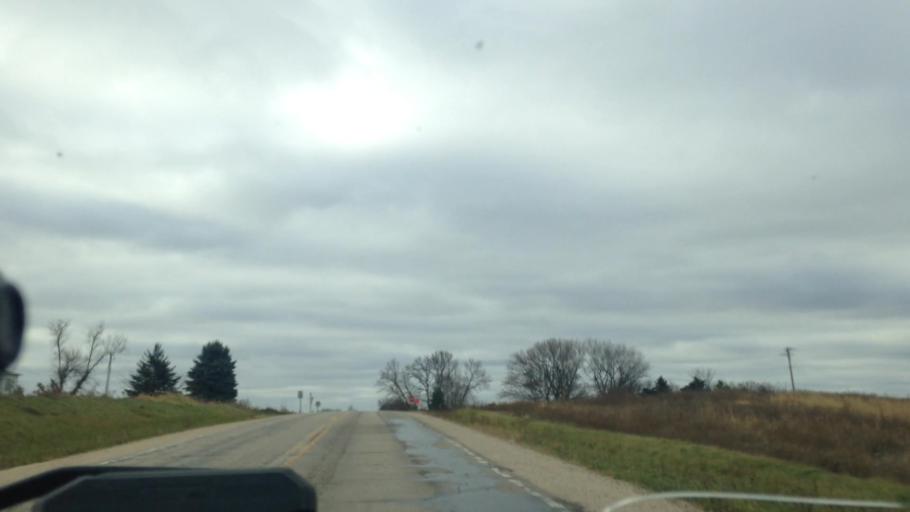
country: US
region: Wisconsin
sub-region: Dodge County
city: Mayville
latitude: 43.4442
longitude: -88.5001
